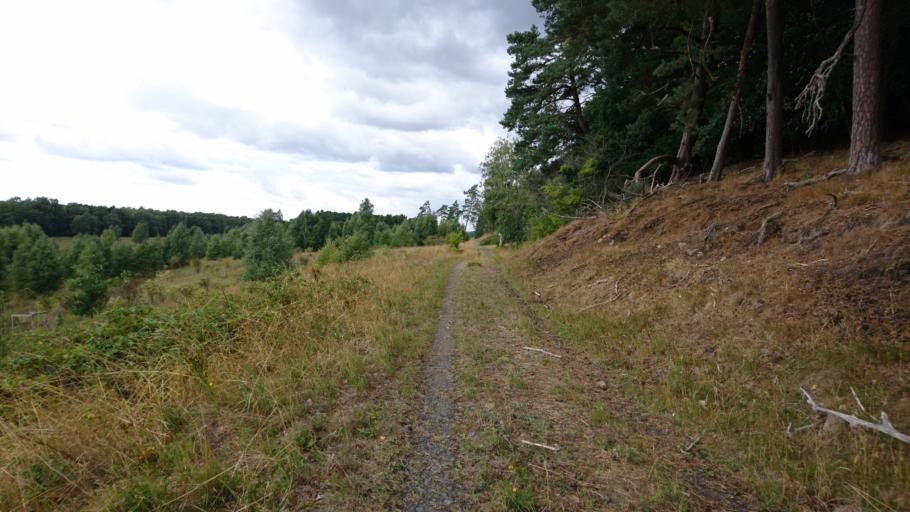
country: SE
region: Skane
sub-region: Sjobo Kommun
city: Sjoebo
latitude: 55.5917
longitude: 13.7721
